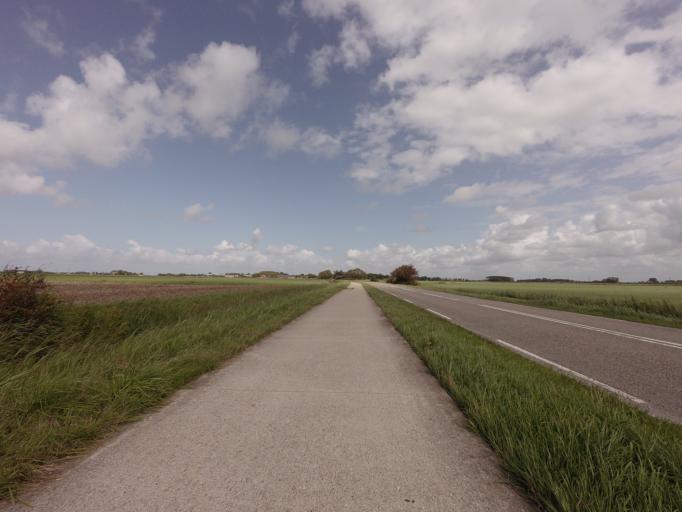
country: NL
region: Friesland
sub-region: Gemeente Harlingen
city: Harlingen
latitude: 53.1406
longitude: 5.4755
